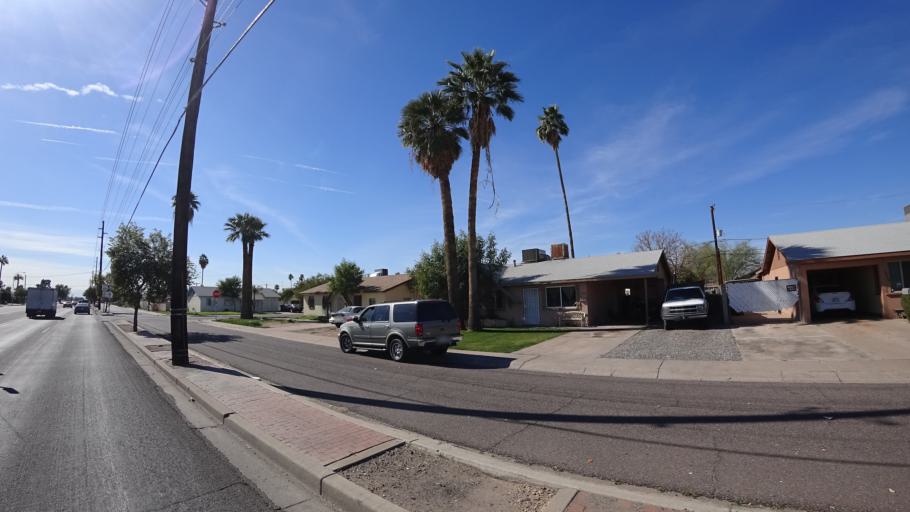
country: US
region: Arizona
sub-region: Maricopa County
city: Glendale
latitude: 33.4871
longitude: -112.1865
